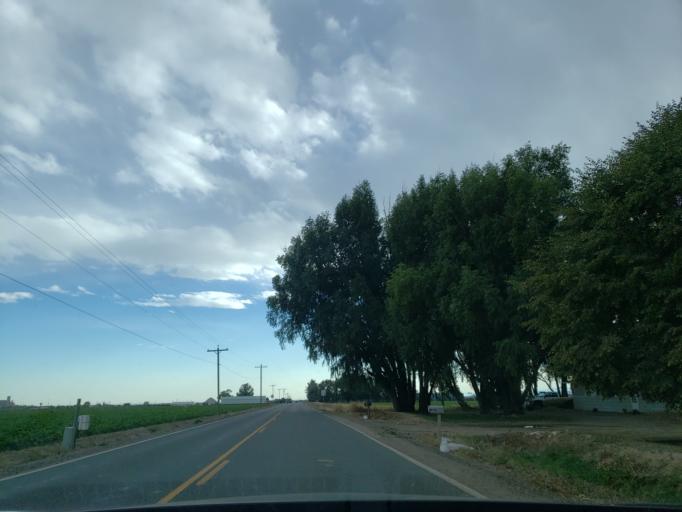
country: US
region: Colorado
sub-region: Larimer County
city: Wellington
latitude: 40.6383
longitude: -105.0197
